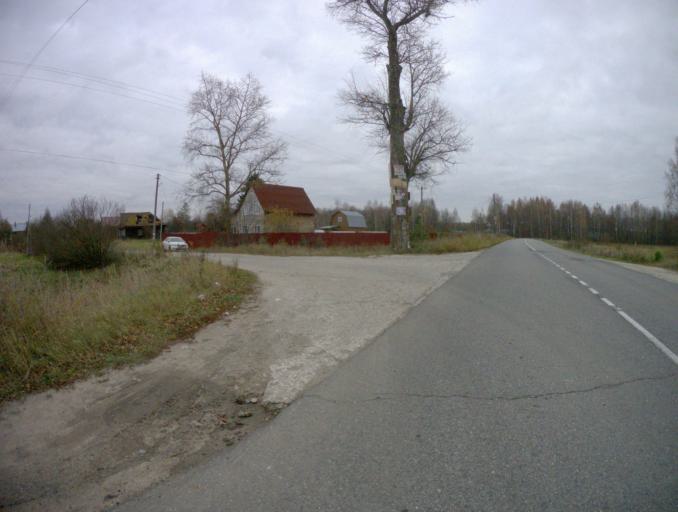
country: RU
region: Moskovskaya
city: Malaya Dubna
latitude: 55.9876
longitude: 38.9438
